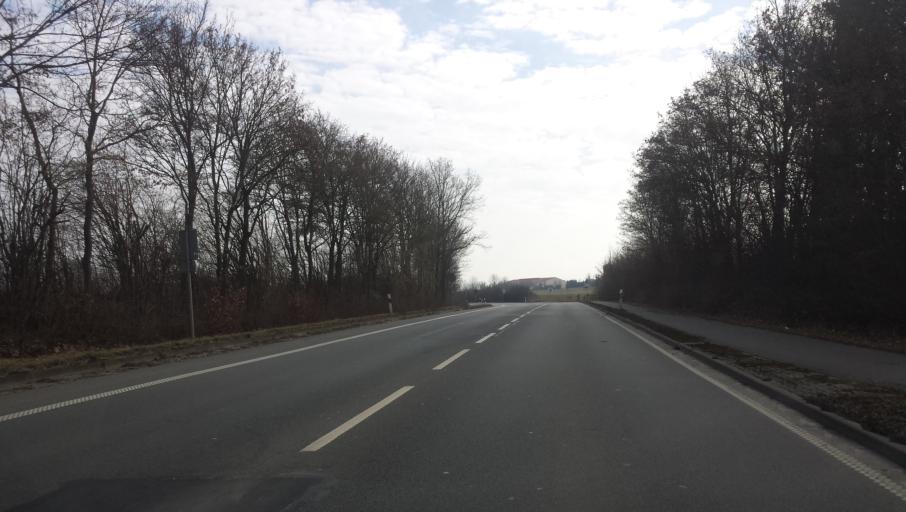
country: DE
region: Hesse
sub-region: Regierungsbezirk Darmstadt
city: Rossdorf
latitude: 49.8601
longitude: 8.7730
